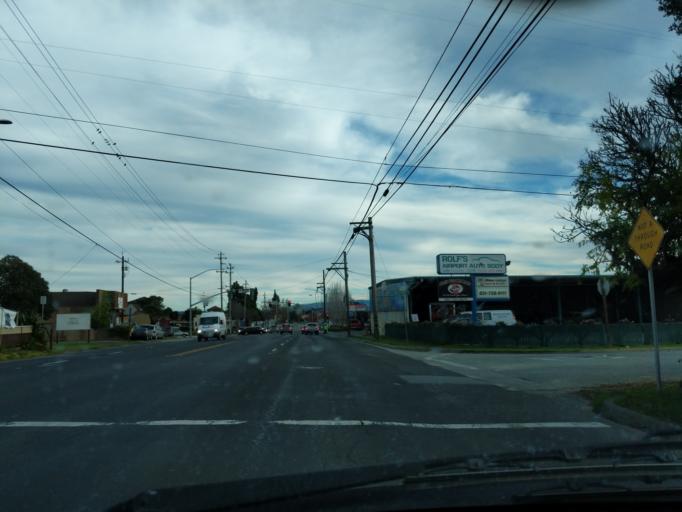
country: US
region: California
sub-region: Santa Cruz County
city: Freedom
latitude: 36.9389
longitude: -121.7790
